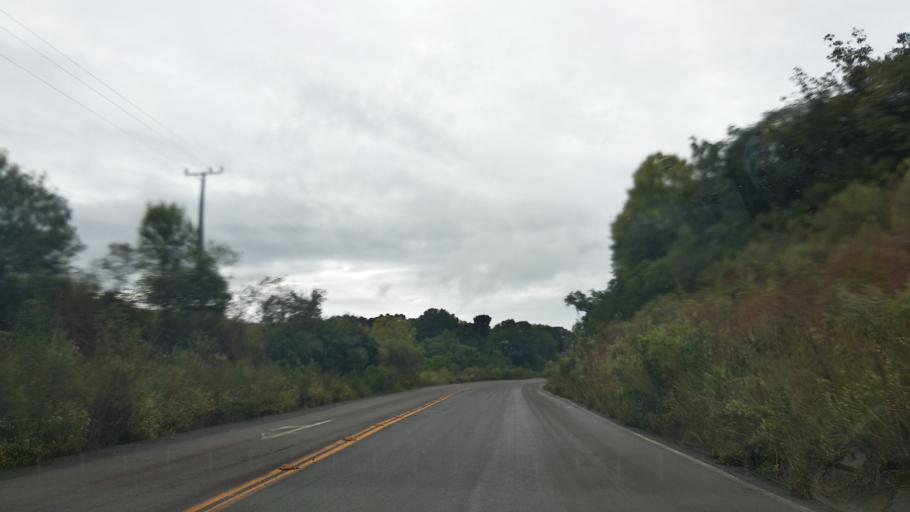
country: BR
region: Santa Catarina
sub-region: Videira
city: Videira
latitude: -27.0167
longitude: -51.1668
